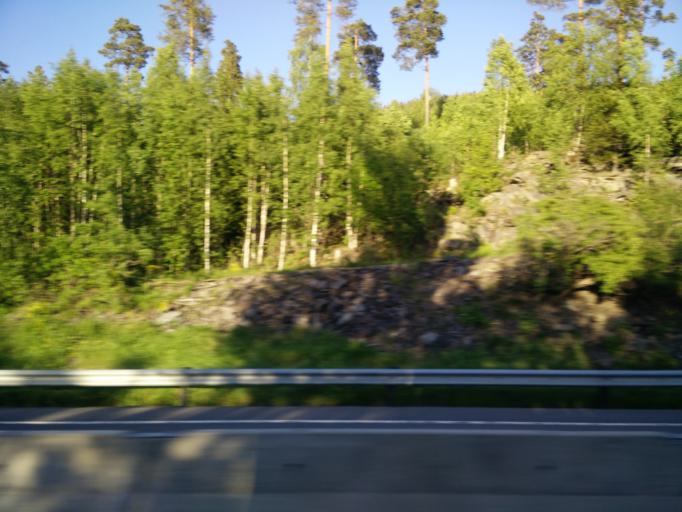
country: NO
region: Buskerud
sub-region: Hole
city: Vik
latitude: 60.0453
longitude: 10.2763
